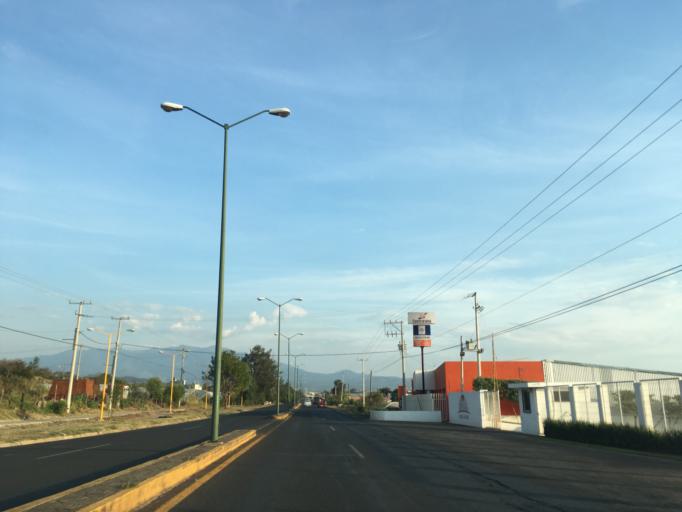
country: MX
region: Michoacan
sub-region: Los Reyes
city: La Higuerita (Colonia San Rafael)
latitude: 19.6099
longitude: -102.4809
